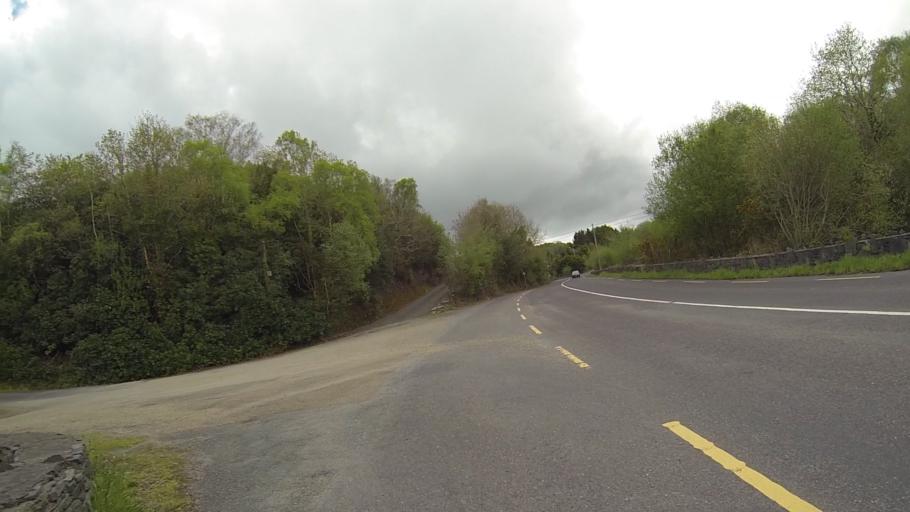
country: IE
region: Munster
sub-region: County Cork
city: Bantry
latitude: 51.7331
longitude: -9.5592
